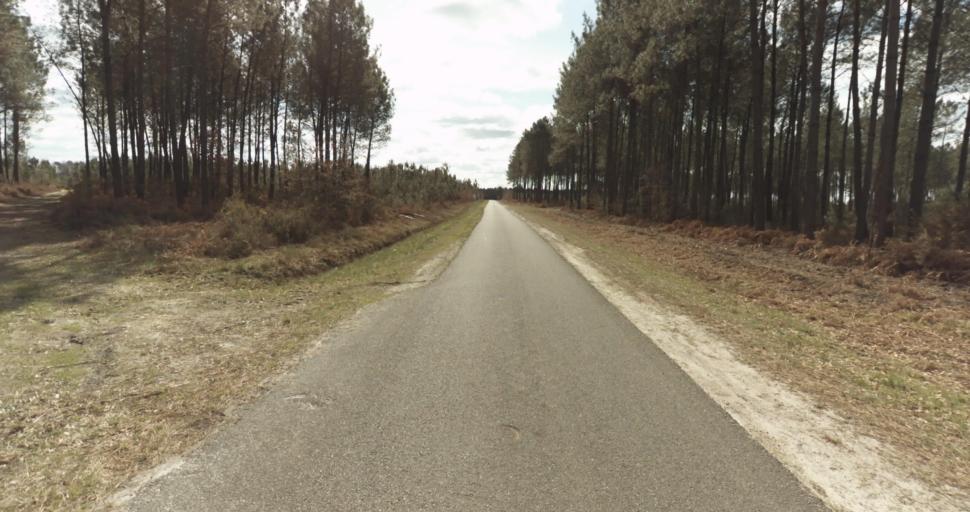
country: FR
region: Aquitaine
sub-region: Departement des Landes
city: Roquefort
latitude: 44.0375
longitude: -0.4232
